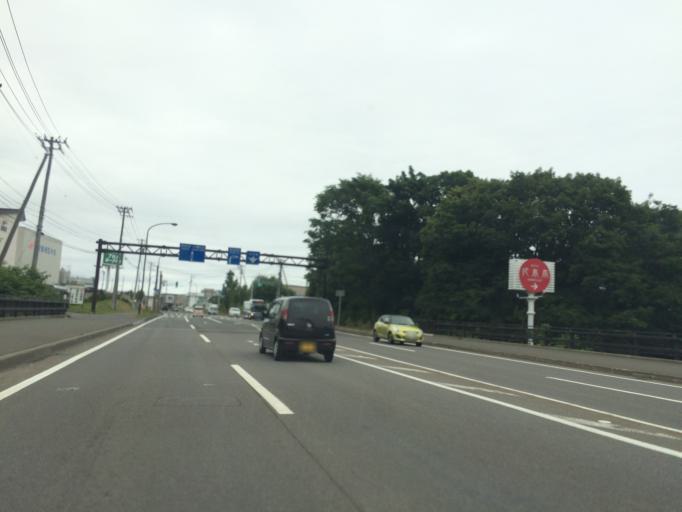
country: JP
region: Hokkaido
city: Otaru
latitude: 43.1413
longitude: 141.1512
